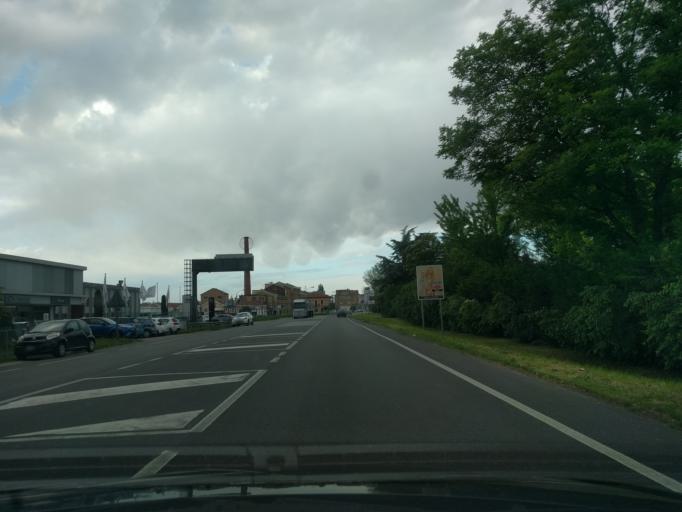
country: IT
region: Veneto
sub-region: Provincia di Rovigo
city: Santa Maria Maddalena
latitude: 44.8777
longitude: 11.6054
